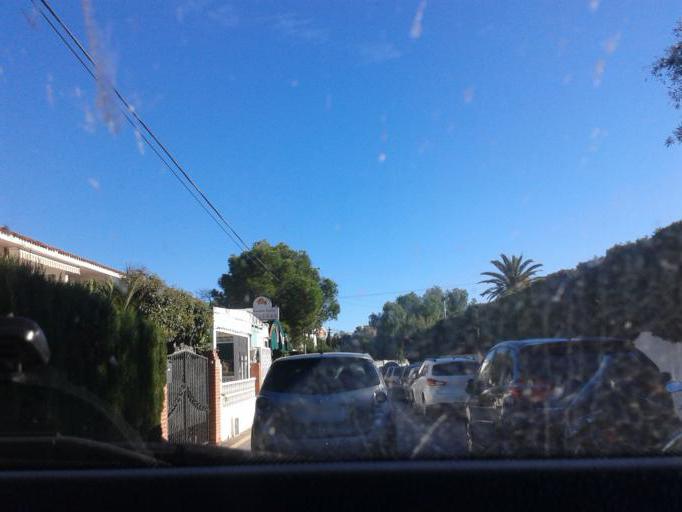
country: ES
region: Valencia
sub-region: Provincia de Alicante
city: el Campello
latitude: 38.4113
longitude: -0.4080
